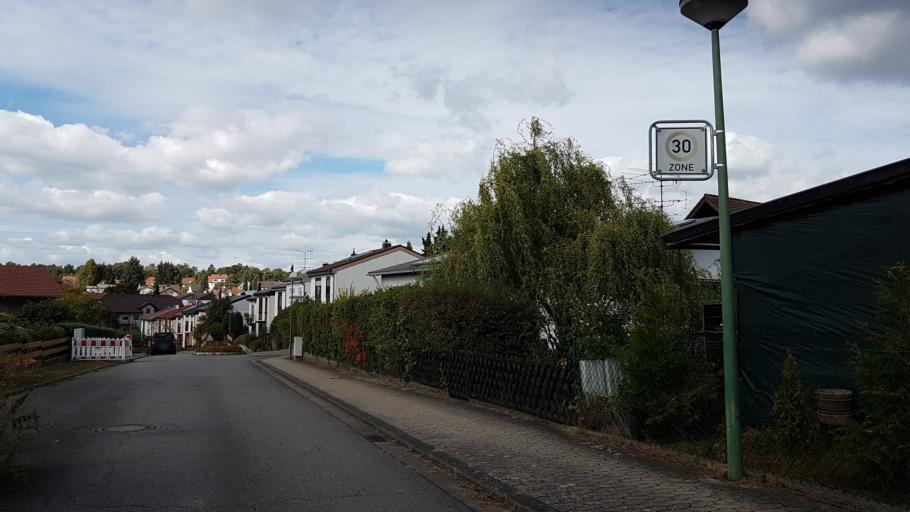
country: DE
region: Saarland
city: Kirkel
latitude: 49.2842
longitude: 7.2385
